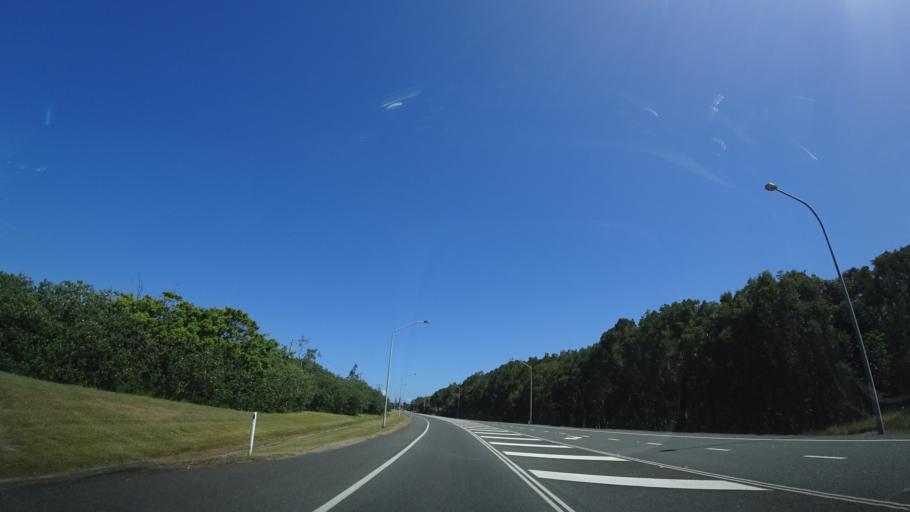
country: AU
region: Queensland
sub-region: Sunshine Coast
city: Coolum Beach
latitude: -26.5771
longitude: 153.0912
